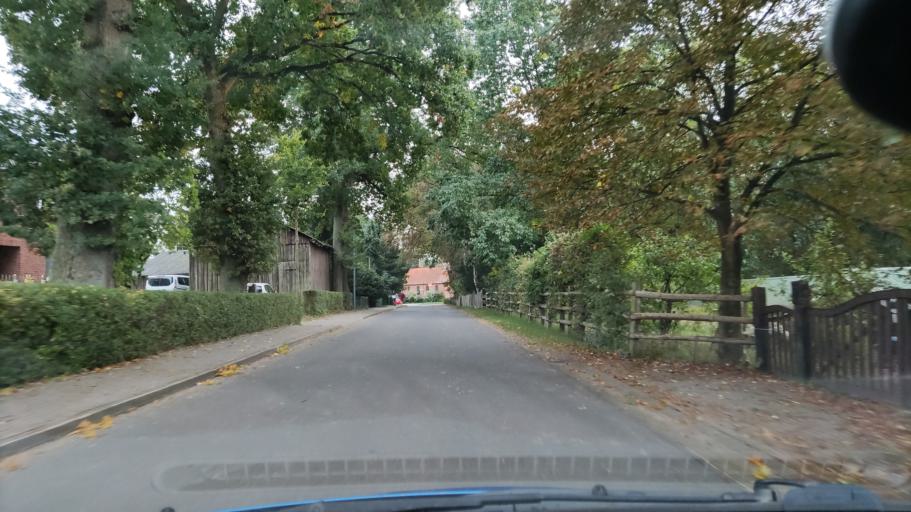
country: DE
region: Lower Saxony
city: Karwitz
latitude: 53.0905
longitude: 11.0073
